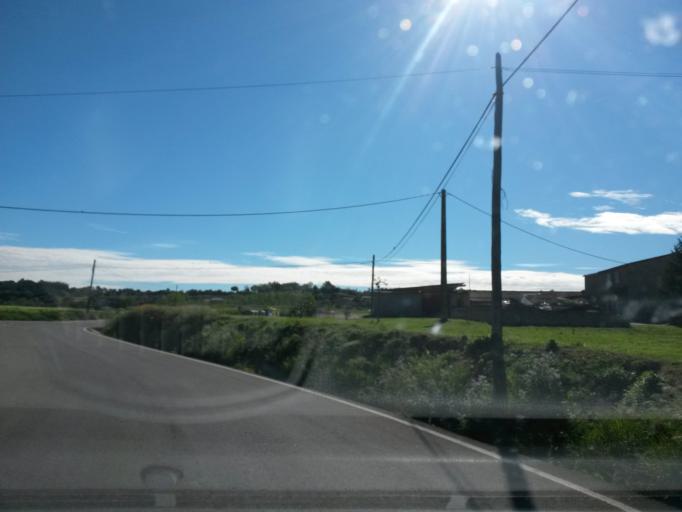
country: ES
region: Catalonia
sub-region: Provincia de Girona
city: Juia
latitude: 42.0218
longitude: 2.9078
